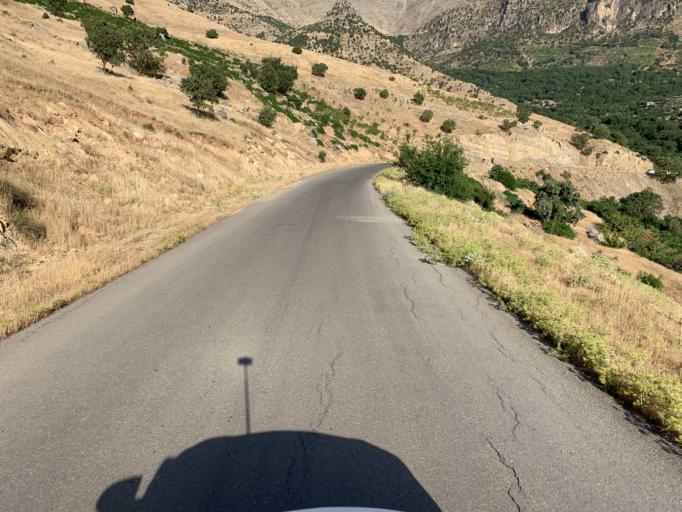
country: IQ
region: As Sulaymaniyah
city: Qeladize
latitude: 35.9945
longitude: 45.1938
